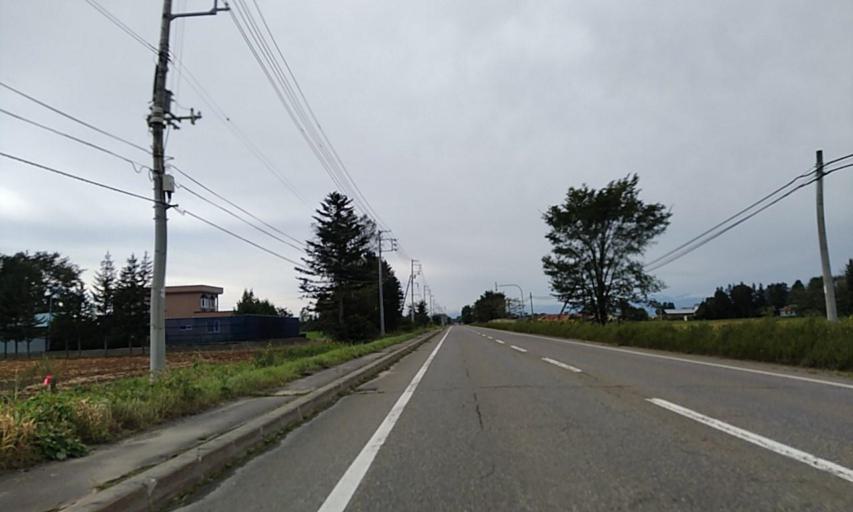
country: JP
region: Hokkaido
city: Obihiro
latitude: 42.8297
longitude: 143.1870
